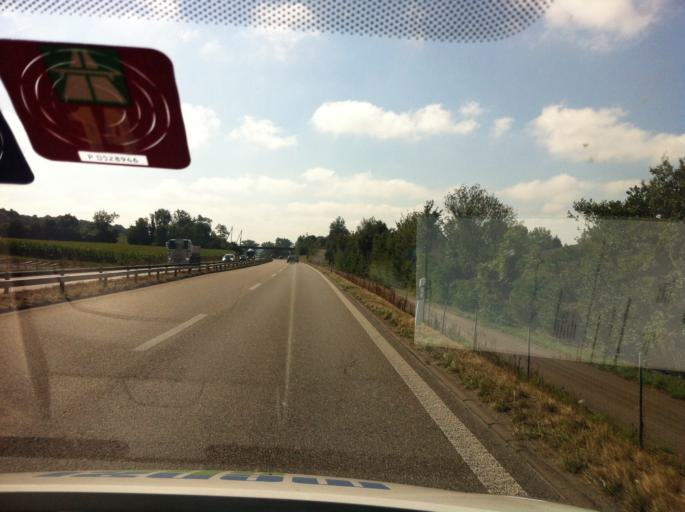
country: CH
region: Zurich
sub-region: Bezirk Buelach
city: Bachenbulach
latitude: 47.4775
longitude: 8.5522
